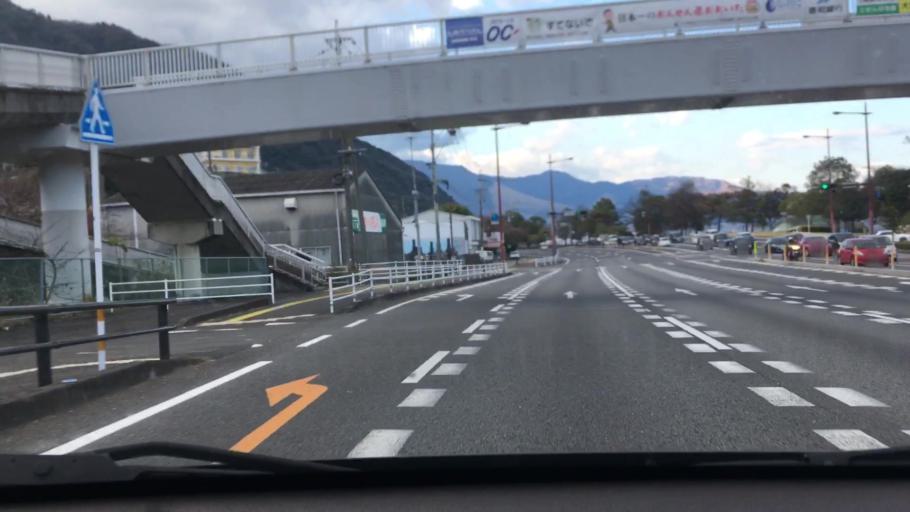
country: JP
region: Oita
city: Beppu
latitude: 33.2557
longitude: 131.5452
